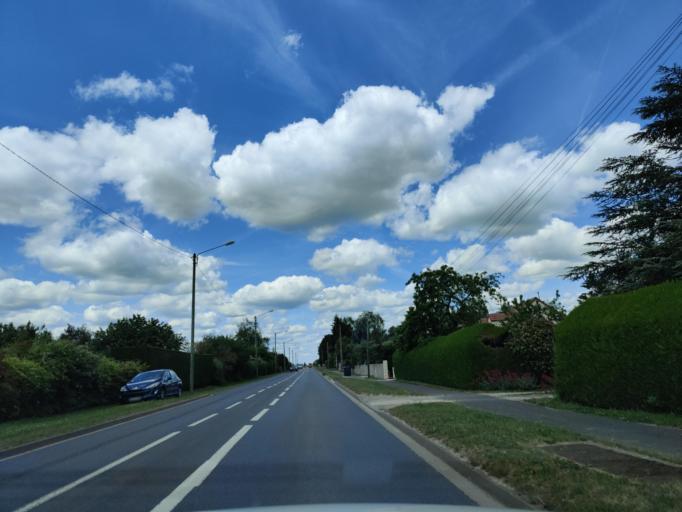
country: FR
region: Centre
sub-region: Departement du Loiret
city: Dadonville
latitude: 48.1428
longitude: 2.2563
